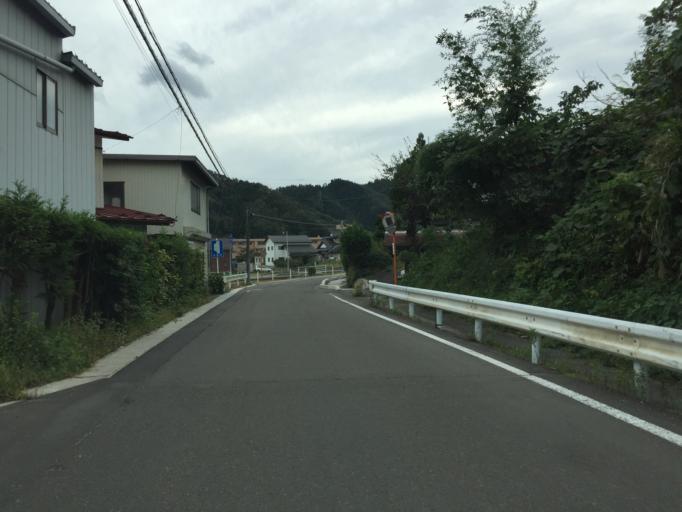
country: JP
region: Miyagi
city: Marumori
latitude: 37.9085
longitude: 140.7620
